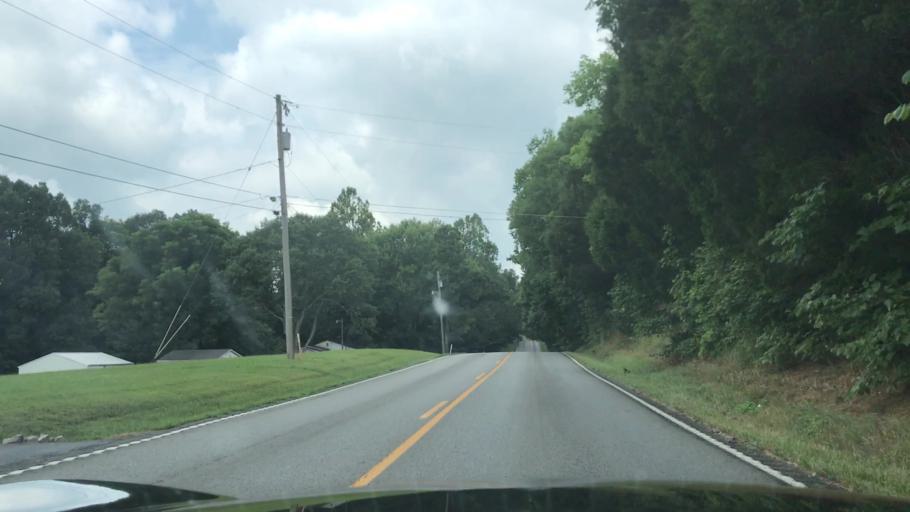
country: US
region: Kentucky
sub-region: Muhlenberg County
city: Greenville
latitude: 37.2032
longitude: -87.0895
